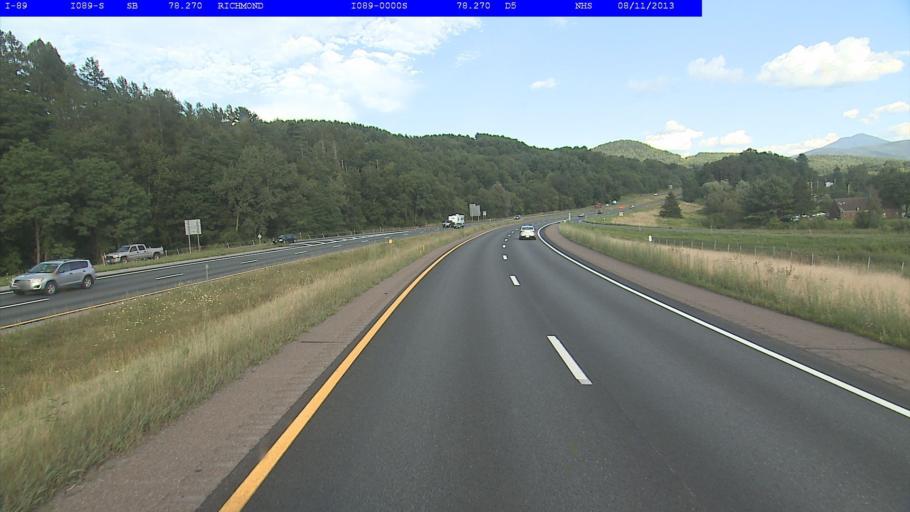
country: US
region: Vermont
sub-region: Chittenden County
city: Williston
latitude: 44.4230
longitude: -73.0083
